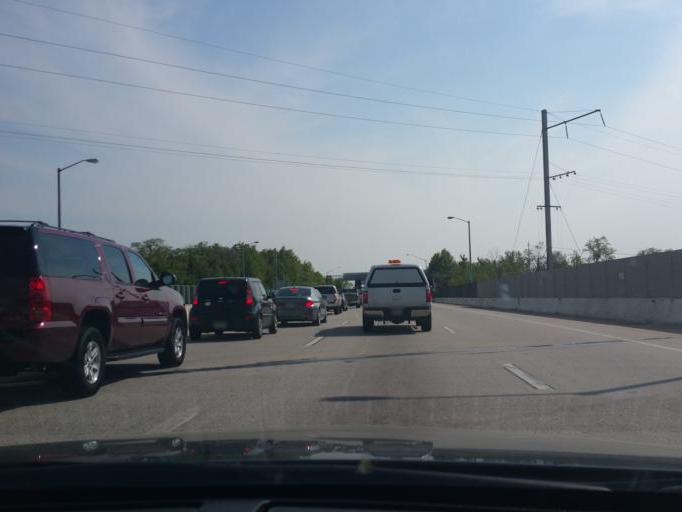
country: US
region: Maryland
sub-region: Baltimore County
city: Rosedale
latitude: 39.2973
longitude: -76.5502
